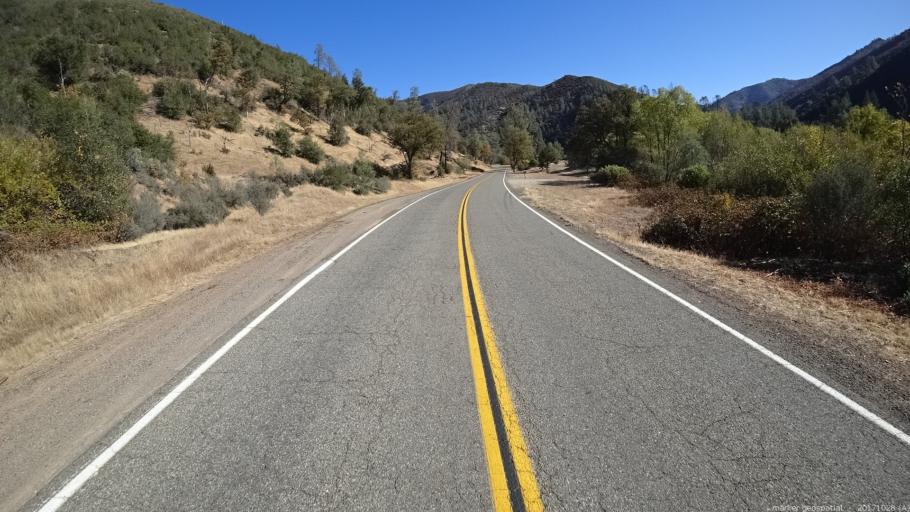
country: US
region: California
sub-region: Trinity County
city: Lewiston
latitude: 40.7173
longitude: -122.6353
